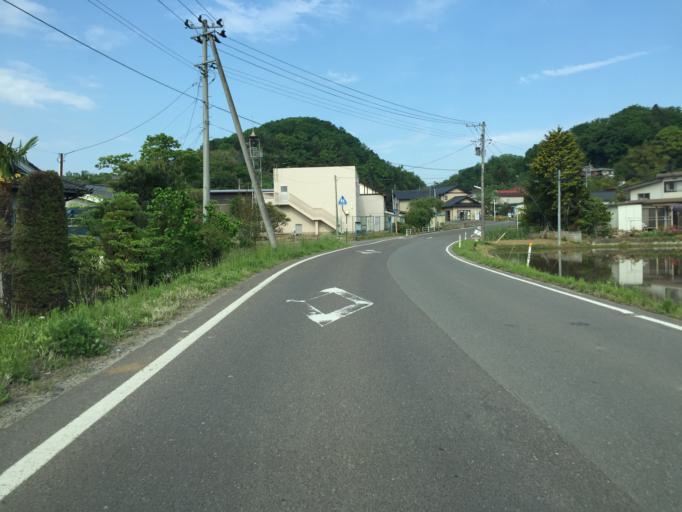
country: JP
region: Fukushima
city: Yanagawamachi-saiwaicho
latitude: 37.7925
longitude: 140.6210
